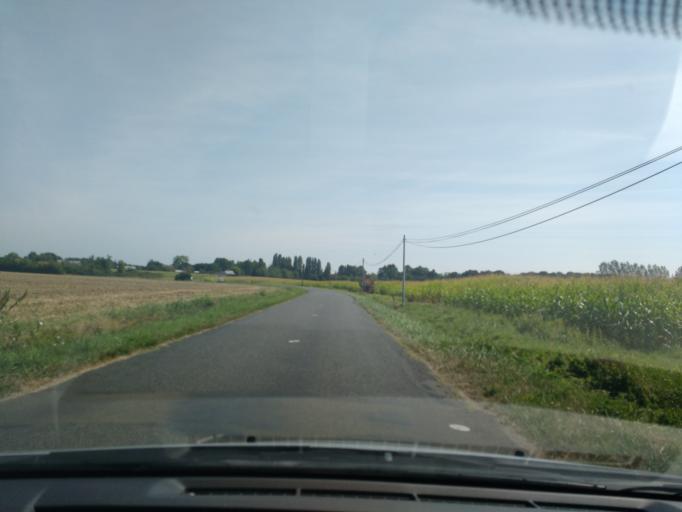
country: FR
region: Pays de la Loire
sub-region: Departement de Maine-et-Loire
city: Maze
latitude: 47.4744
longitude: -0.2544
